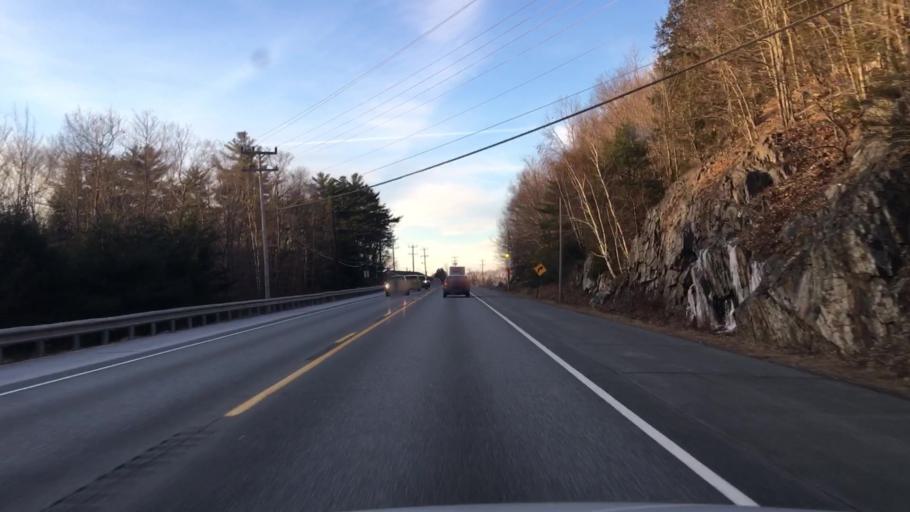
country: US
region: Maine
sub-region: Hancock County
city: Dedham
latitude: 44.7248
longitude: -68.6199
